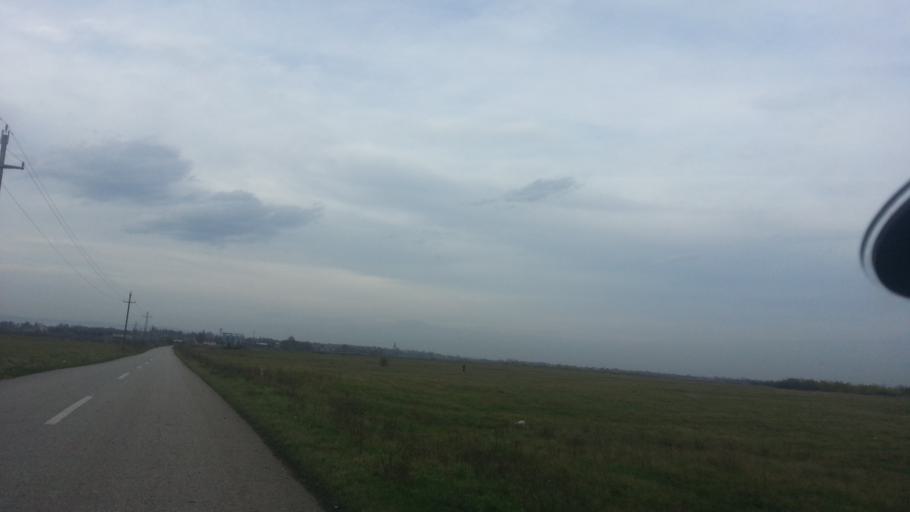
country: RS
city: Putinci
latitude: 44.9708
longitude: 19.9729
